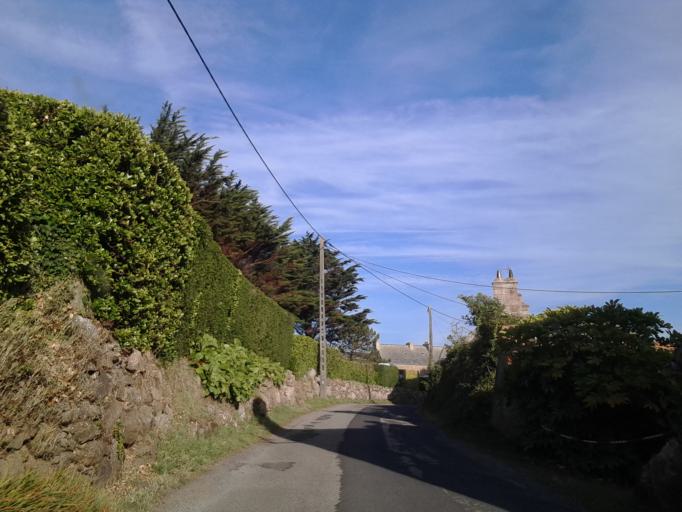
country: FR
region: Lower Normandy
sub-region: Departement de la Manche
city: Fermanville
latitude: 49.6843
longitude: -1.4700
